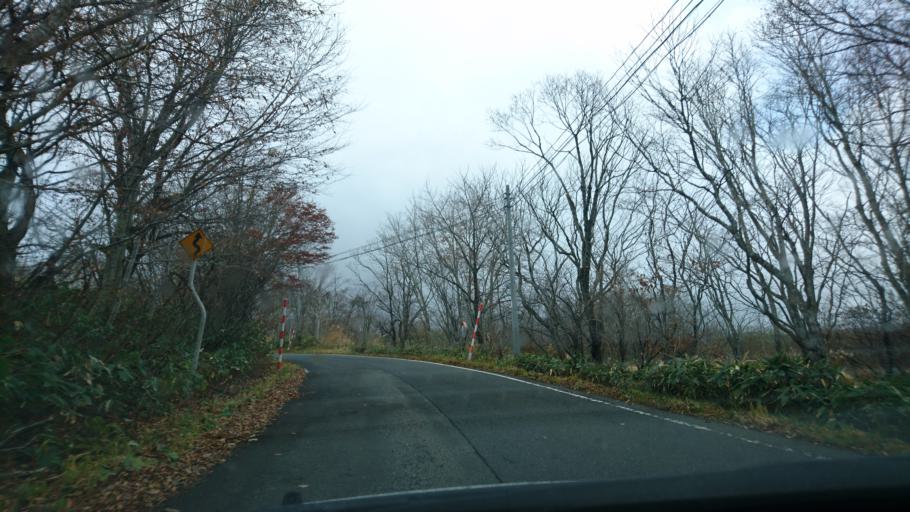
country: JP
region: Iwate
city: Ichinoseki
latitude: 38.9263
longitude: 140.8422
